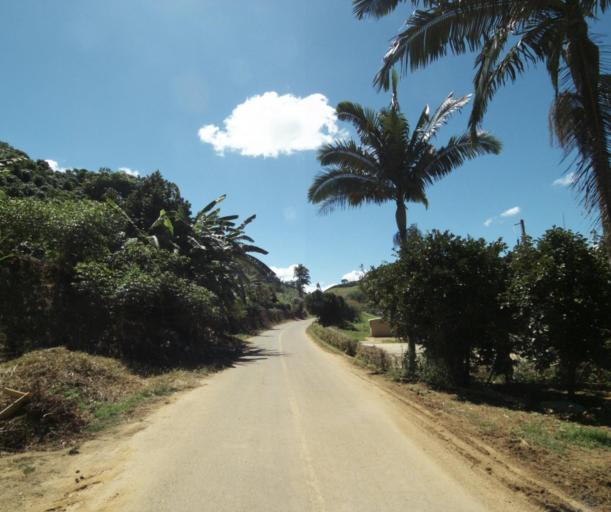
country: BR
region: Minas Gerais
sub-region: Espera Feliz
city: Espera Feliz
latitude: -20.6392
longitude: -41.8152
